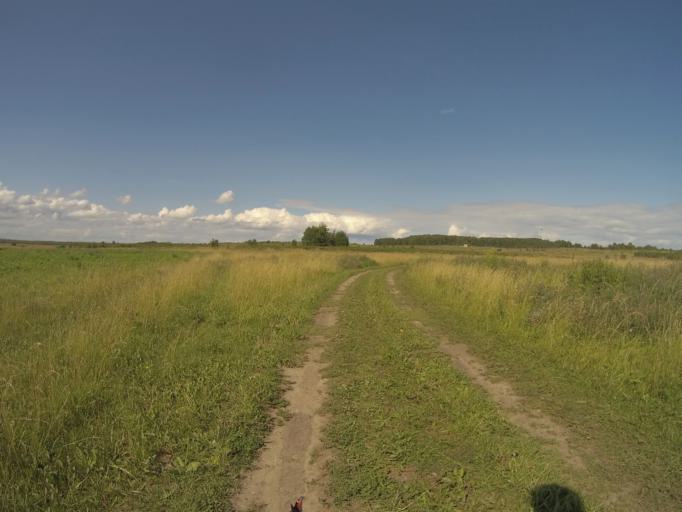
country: RU
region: Vladimir
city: Vladimir
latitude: 56.2894
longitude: 40.3494
